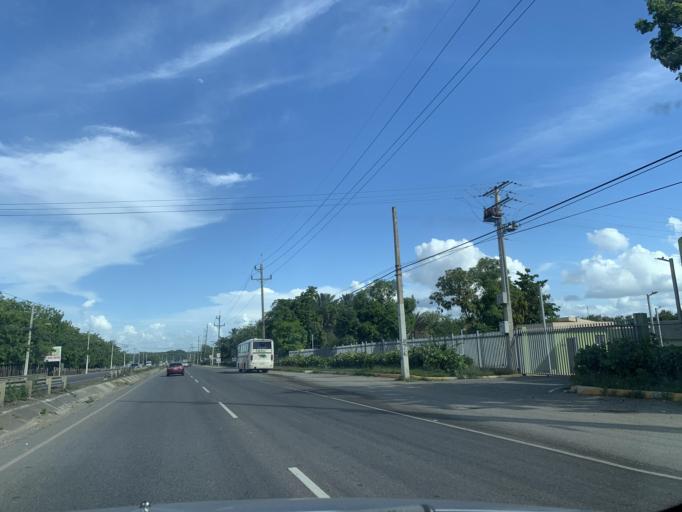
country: DO
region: Santiago
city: Villa Gonzalez
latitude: 19.5293
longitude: -70.7760
